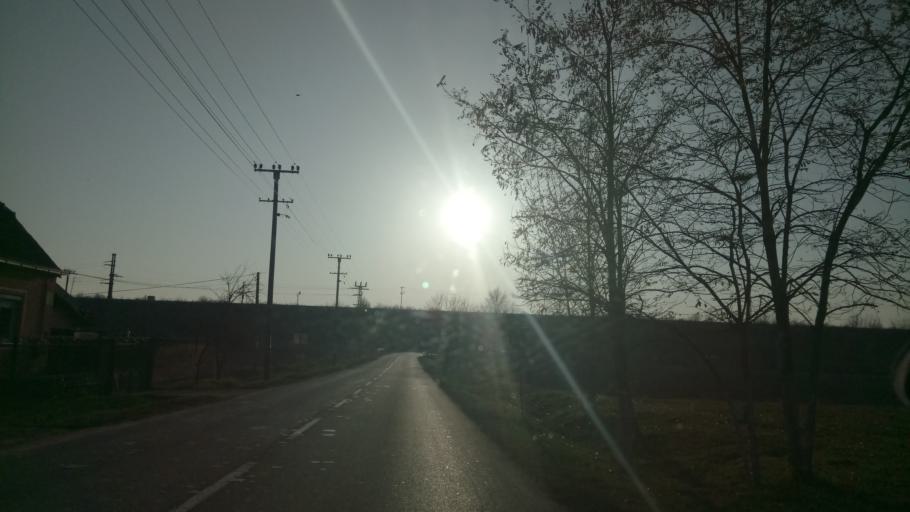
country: RS
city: Beska
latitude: 45.1222
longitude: 20.0616
